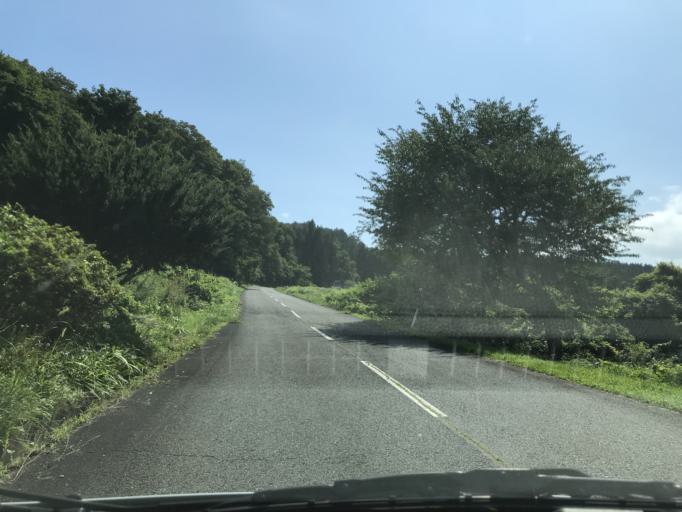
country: JP
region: Iwate
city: Ofunato
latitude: 38.9928
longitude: 141.4287
